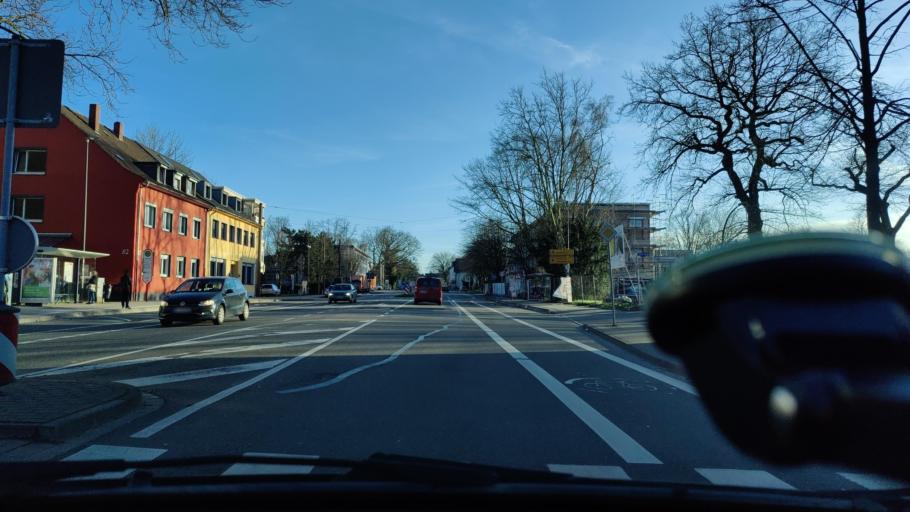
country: DE
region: North Rhine-Westphalia
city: Castrop-Rauxel
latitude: 51.5590
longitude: 7.3100
